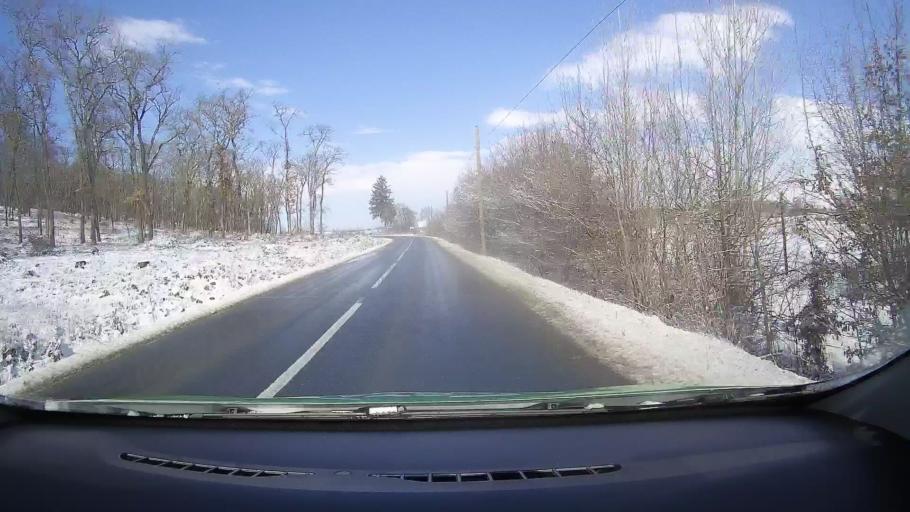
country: RO
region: Sibiu
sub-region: Comuna Nocrich
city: Nocrich
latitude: 45.8640
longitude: 24.4545
